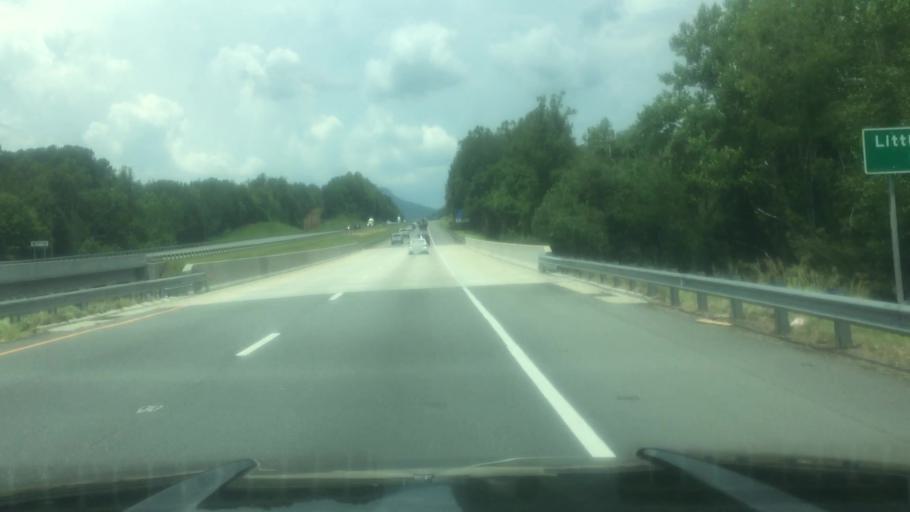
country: US
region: North Carolina
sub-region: Stokes County
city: King
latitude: 36.3016
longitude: -80.4150
